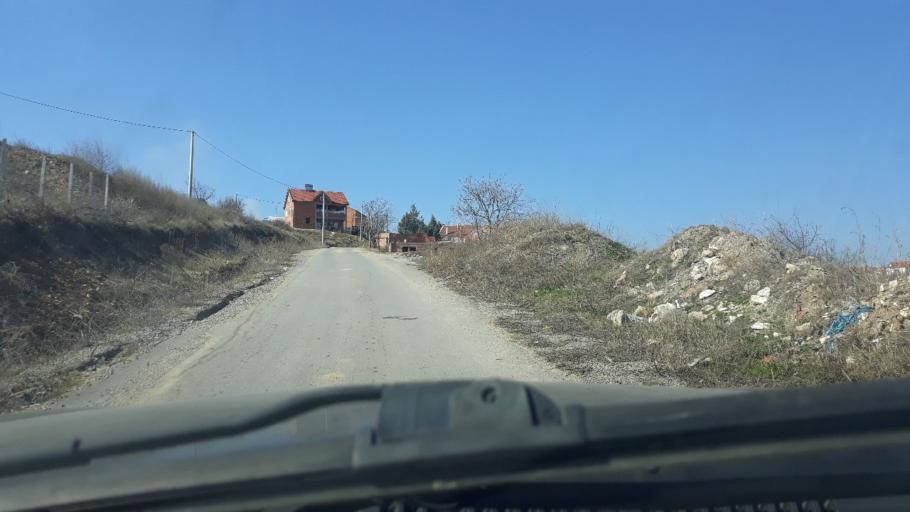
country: MK
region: Veles
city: Gorno Orizari
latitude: 41.6807
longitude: 21.7358
